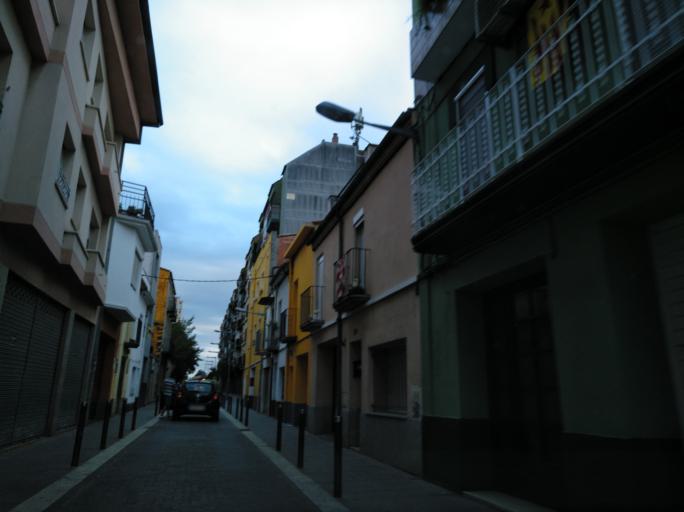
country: ES
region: Catalonia
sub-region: Provincia de Girona
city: Salt
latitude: 41.9757
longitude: 2.7983
